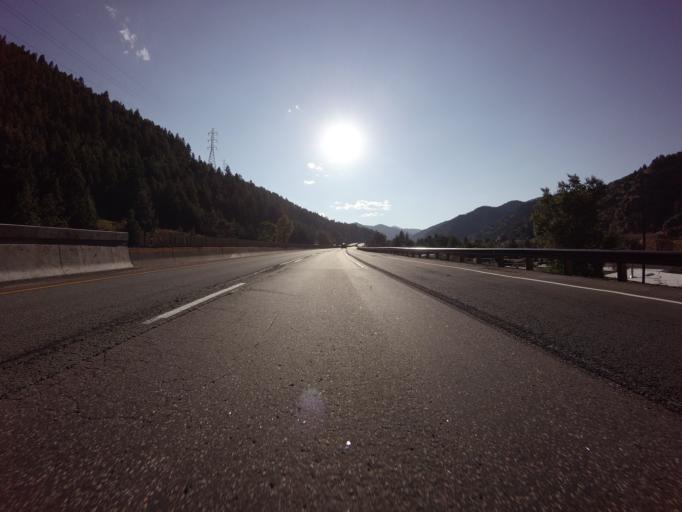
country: US
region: Colorado
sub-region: Clear Creek County
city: Idaho Springs
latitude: 39.7404
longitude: -105.5004
